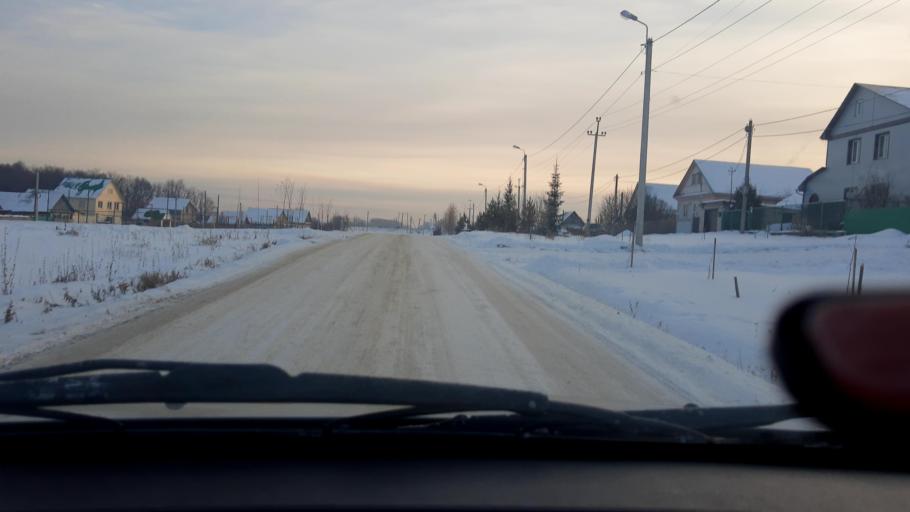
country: RU
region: Bashkortostan
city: Avdon
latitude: 54.7435
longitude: 55.7982
